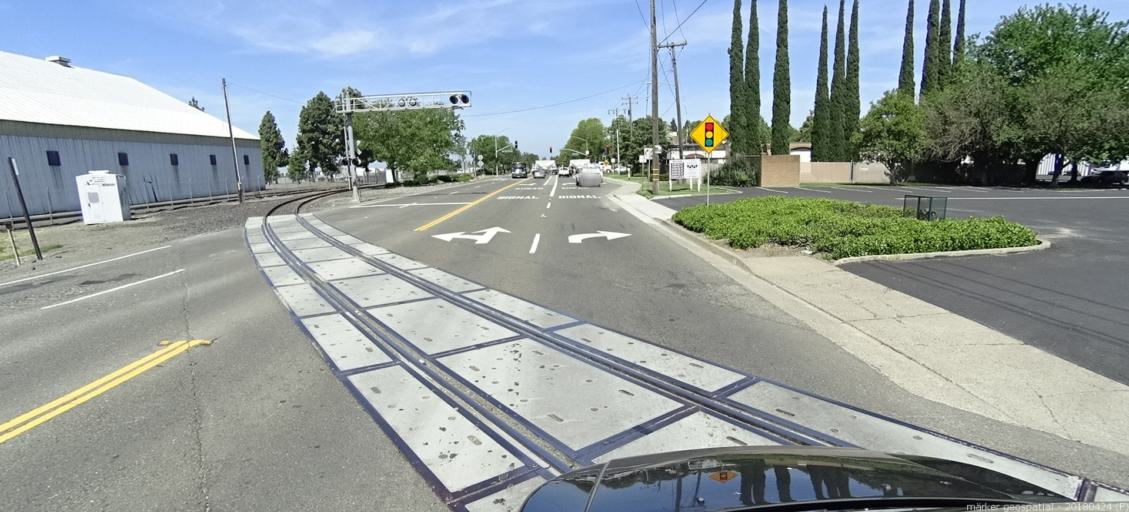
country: US
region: California
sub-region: Yolo County
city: West Sacramento
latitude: 38.5687
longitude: -121.5483
